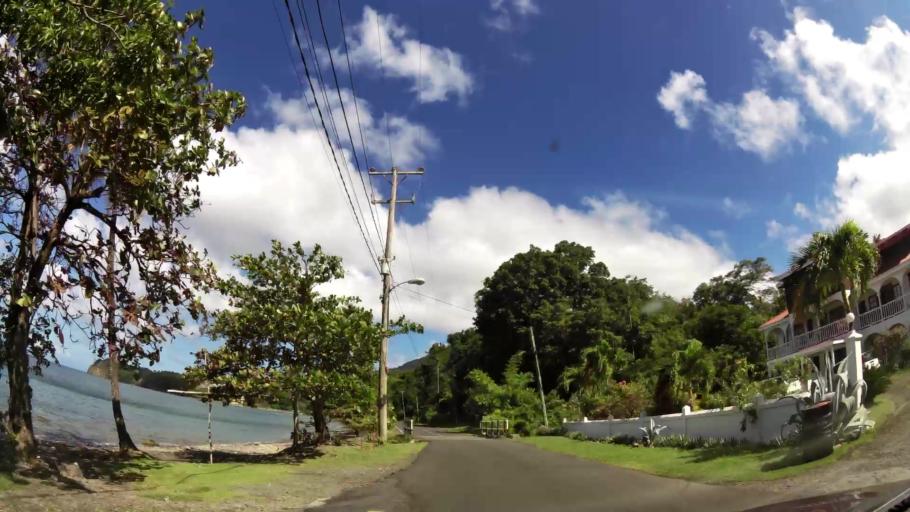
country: DM
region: Saint John
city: Portsmouth
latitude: 15.5939
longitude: -61.4631
